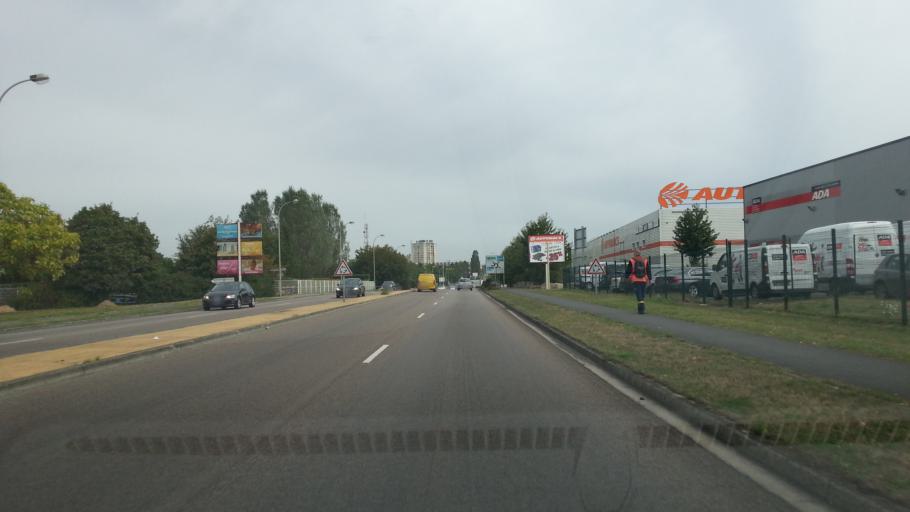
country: FR
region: Picardie
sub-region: Departement de l'Oise
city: Creil
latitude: 49.2425
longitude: 2.4673
